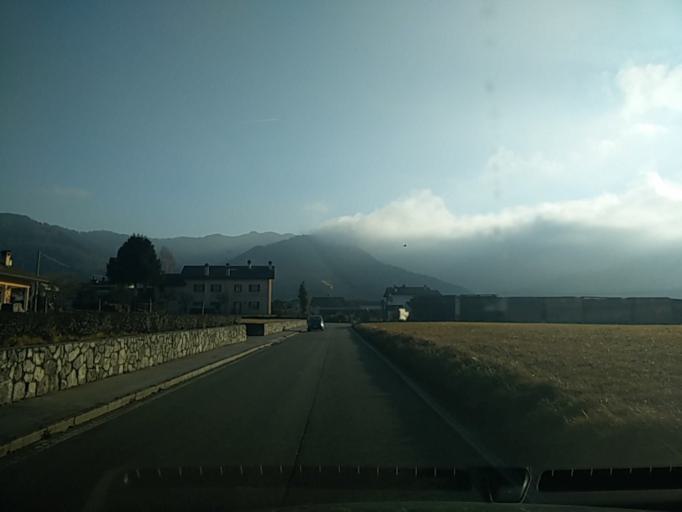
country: IT
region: Veneto
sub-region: Provincia di Belluno
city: Trichiana
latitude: 46.0418
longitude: 12.1593
